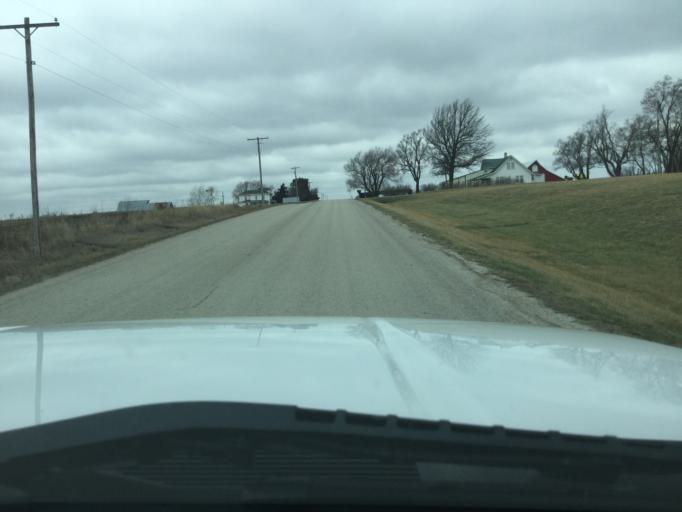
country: US
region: Kansas
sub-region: Nemaha County
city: Seneca
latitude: 39.7400
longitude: -96.0131
